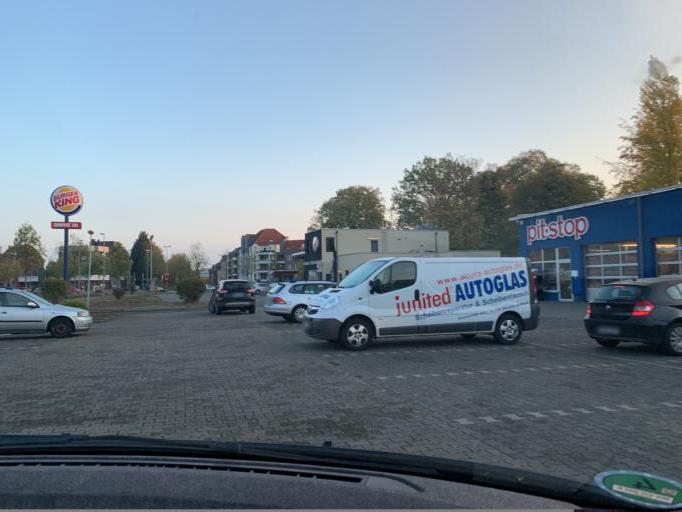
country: DE
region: North Rhine-Westphalia
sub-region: Regierungsbezirk Dusseldorf
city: Monchengladbach
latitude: 51.1523
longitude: 6.4512
